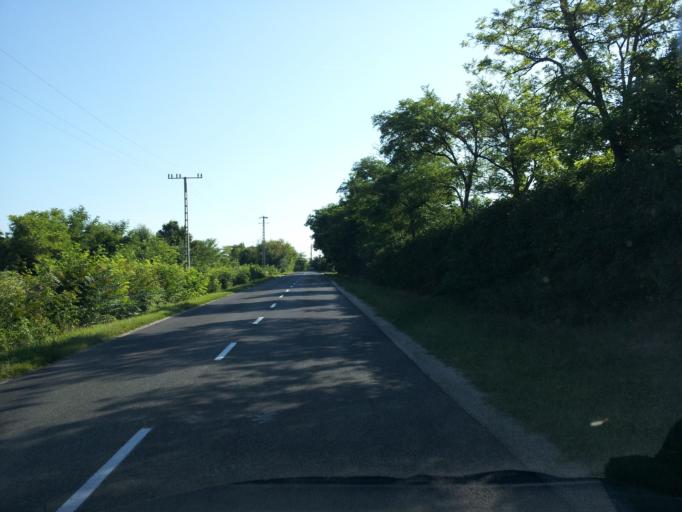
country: HU
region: Veszprem
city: Osi
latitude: 47.1245
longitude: 18.2378
